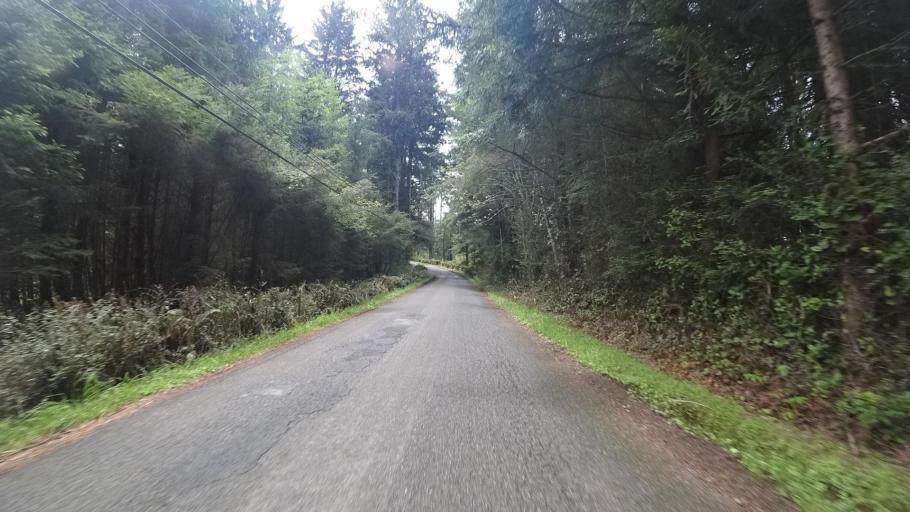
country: US
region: California
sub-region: Humboldt County
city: Bayside
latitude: 40.8518
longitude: -124.0314
